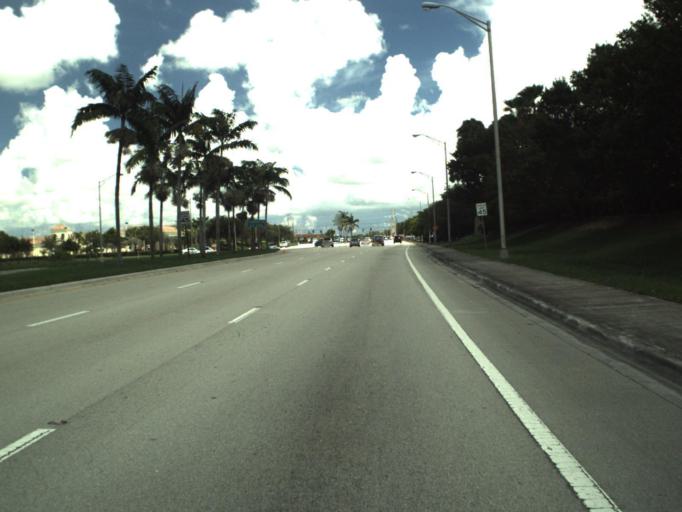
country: US
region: Florida
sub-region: Miami-Dade County
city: Country Club
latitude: 25.9789
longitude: -80.3159
